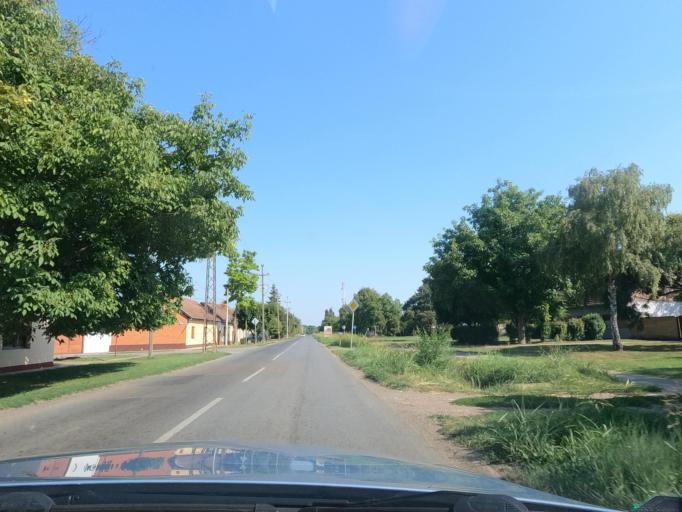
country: RS
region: Autonomna Pokrajina Vojvodina
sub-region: Juznobacki Okrug
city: Becej
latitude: 45.6269
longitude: 20.0253
